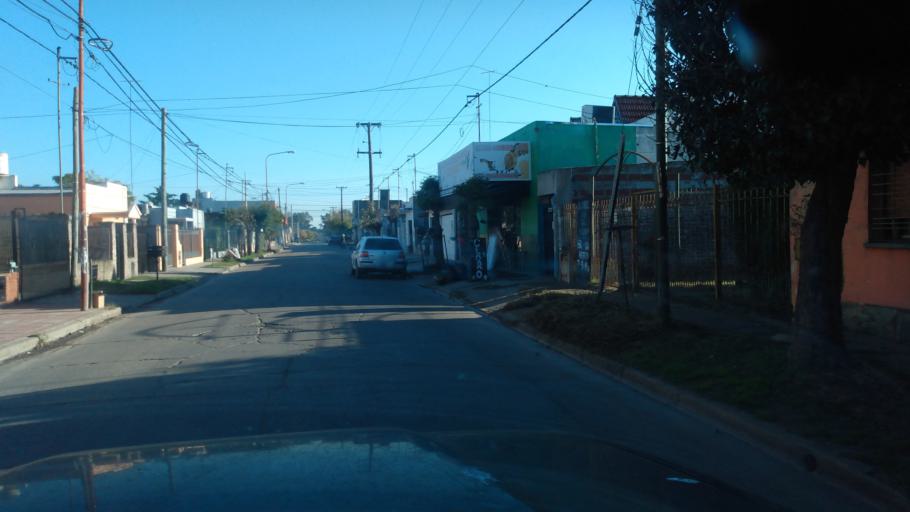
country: AR
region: Buenos Aires
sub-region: Partido de Lujan
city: Lujan
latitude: -34.5655
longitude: -59.0938
